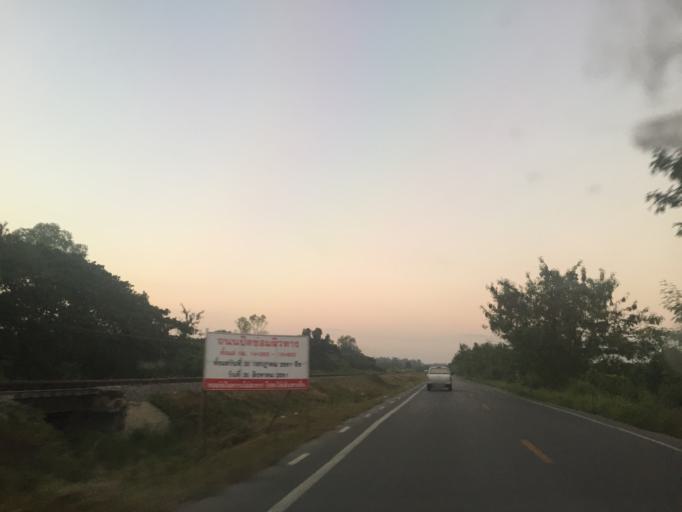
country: TH
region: Chiang Mai
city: Saraphi
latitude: 18.6608
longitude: 99.0446
